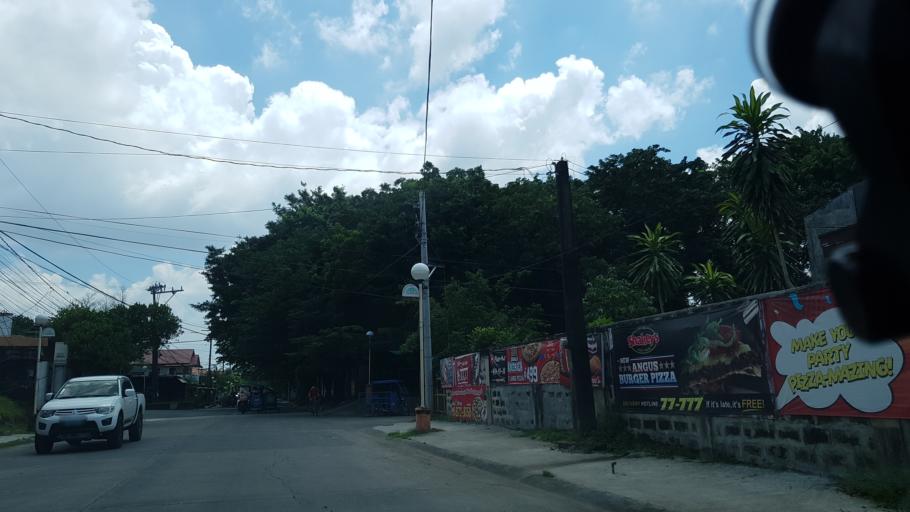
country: PH
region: Calabarzon
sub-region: Province of Rizal
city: Las Pinas
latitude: 14.4344
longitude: 120.9836
